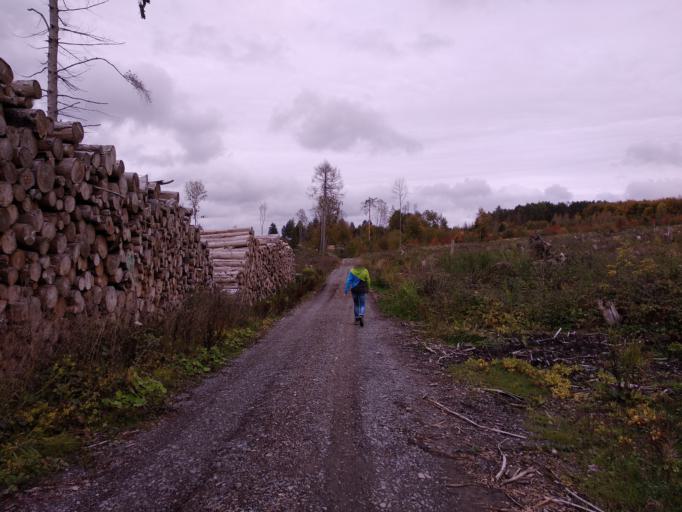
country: DE
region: North Rhine-Westphalia
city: Beverungen
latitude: 51.6723
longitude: 9.3261
